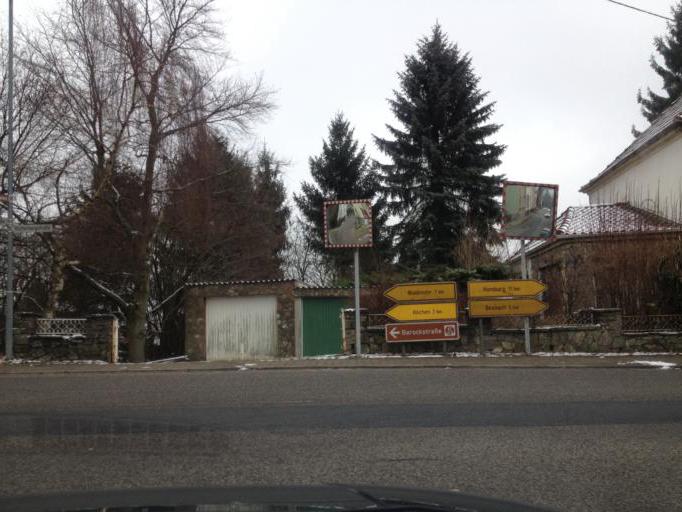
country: DE
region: Saarland
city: Bexbach
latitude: 49.3825
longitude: 7.2571
